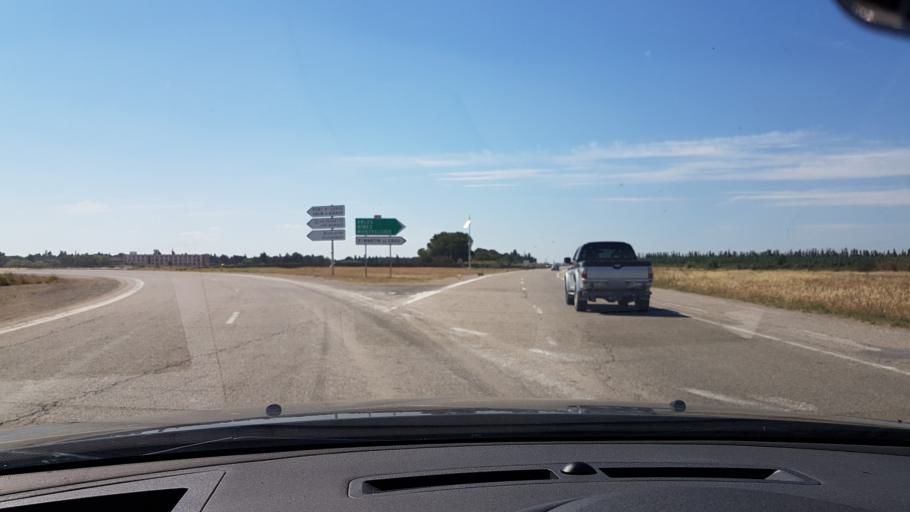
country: FR
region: Provence-Alpes-Cote d'Azur
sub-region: Departement des Bouches-du-Rhone
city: Fos-sur-Mer
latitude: 43.4874
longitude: 4.8861
